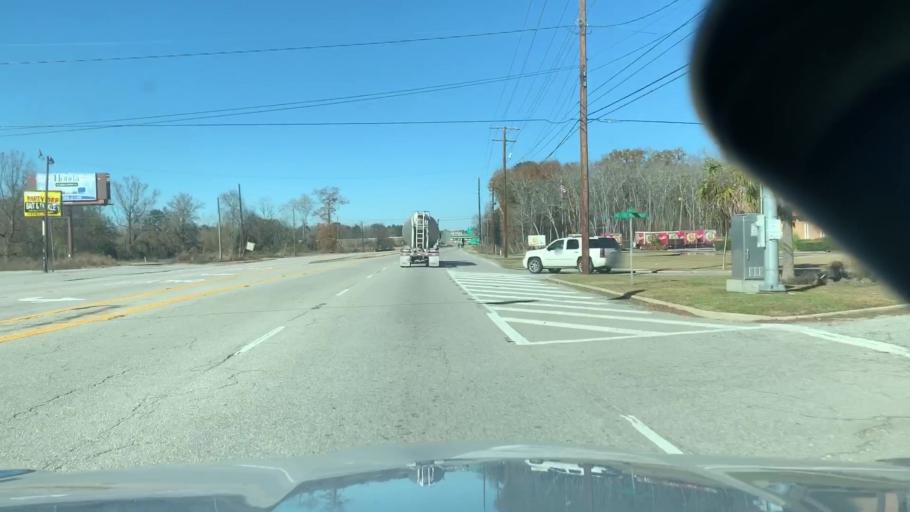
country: US
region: South Carolina
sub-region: Richland County
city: Columbia
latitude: 33.9455
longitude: -80.9873
